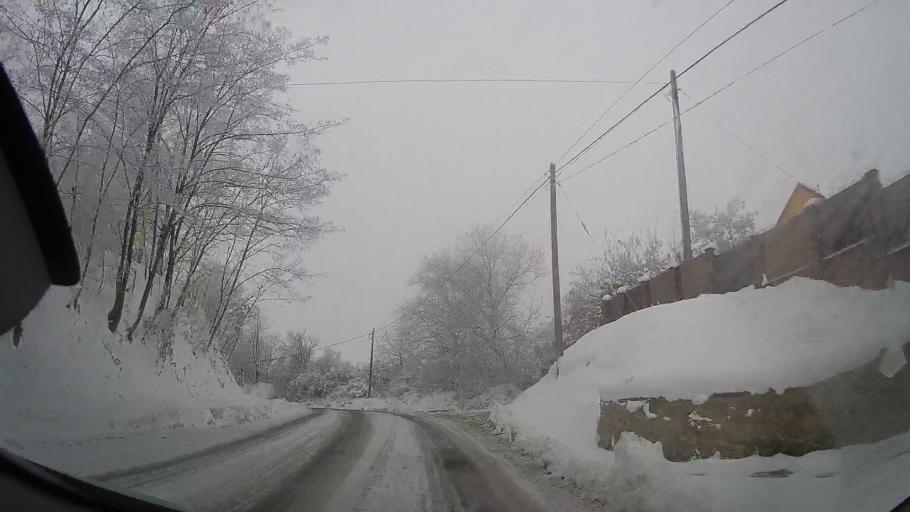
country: RO
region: Neamt
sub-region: Comuna Poenari
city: Poienari
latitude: 46.8900
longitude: 27.1349
